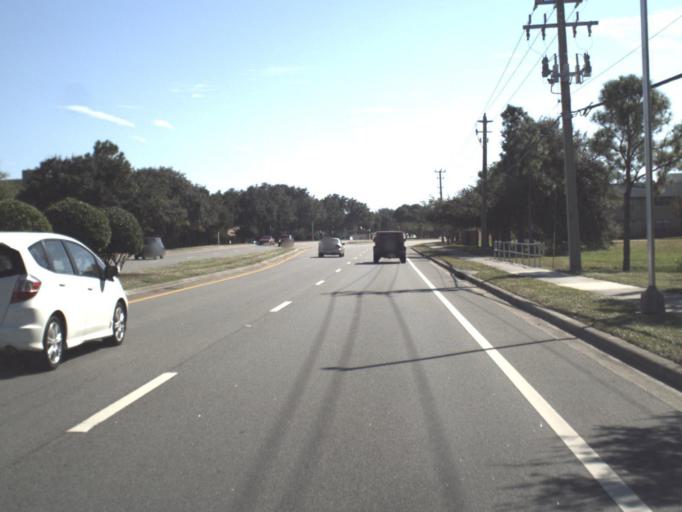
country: US
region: Florida
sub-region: Brevard County
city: South Patrick Shores
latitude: 28.2241
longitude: -80.6773
